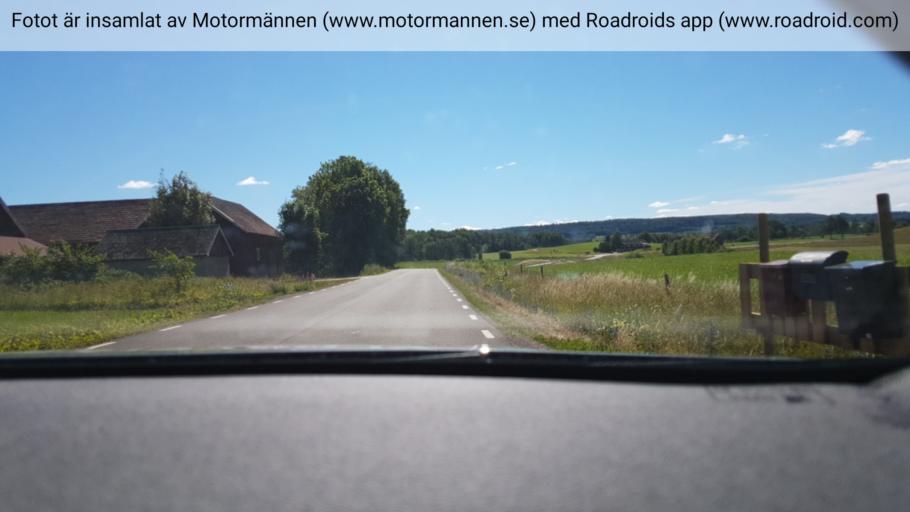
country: SE
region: Vaestra Goetaland
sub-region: Falkopings Kommun
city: Akarp
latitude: 58.2540
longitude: 13.6891
